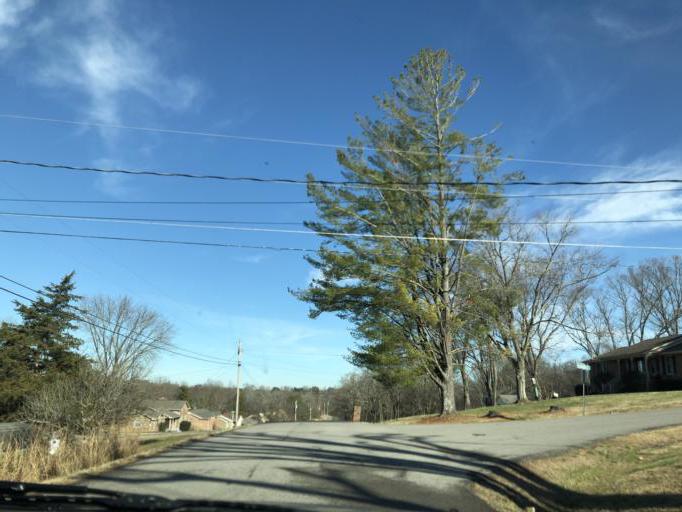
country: US
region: Tennessee
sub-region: Wilson County
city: Mount Juliet
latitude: 36.1783
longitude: -86.5258
